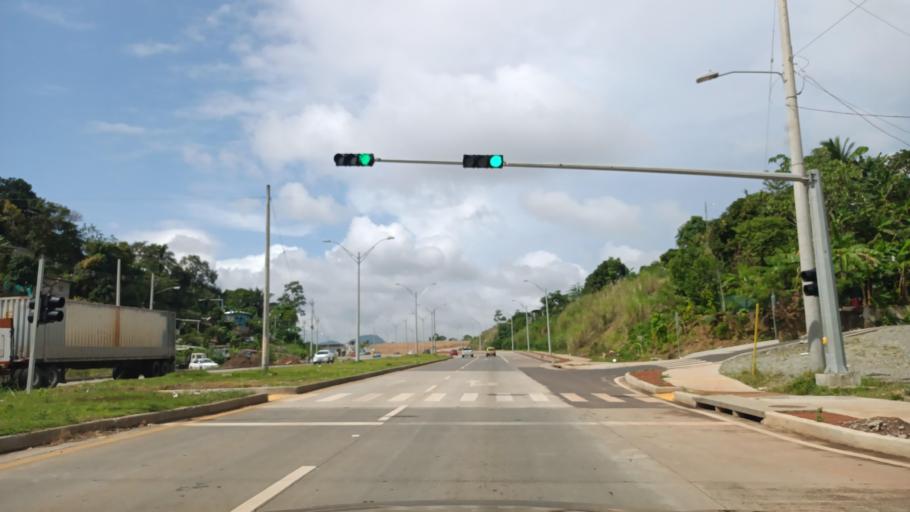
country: PA
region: Panama
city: Las Cumbres
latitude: 9.1022
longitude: -79.4950
